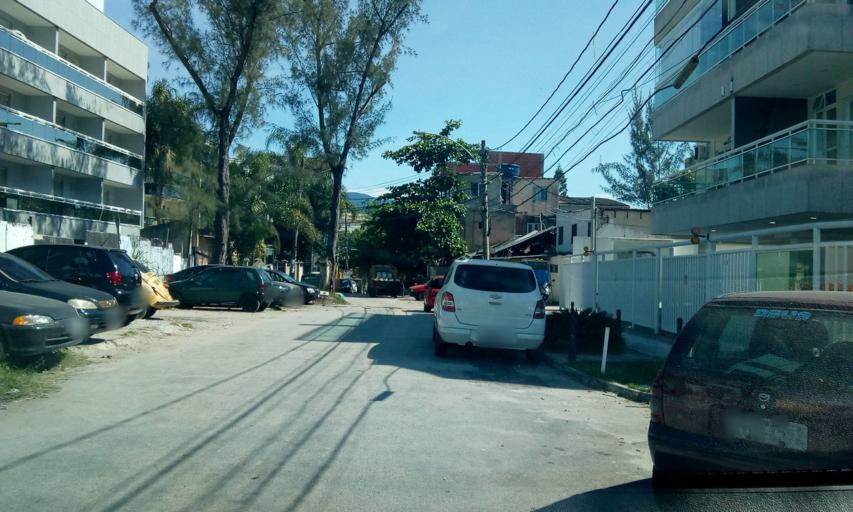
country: BR
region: Rio de Janeiro
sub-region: Nilopolis
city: Nilopolis
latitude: -23.0296
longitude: -43.4739
